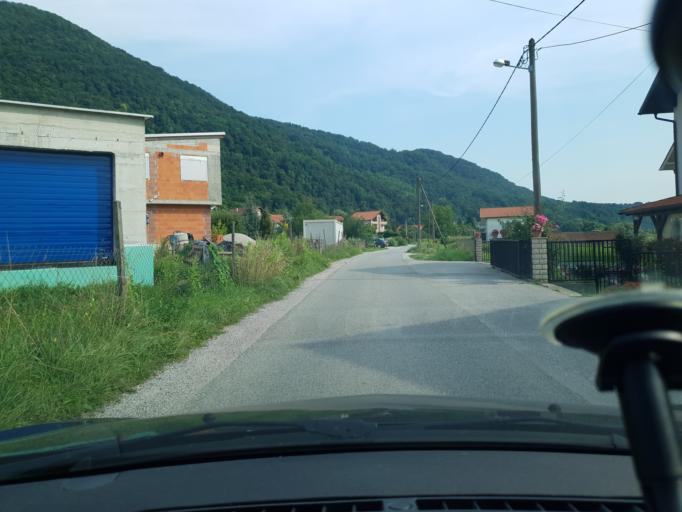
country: HR
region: Zagrebacka
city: Jablanovec
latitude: 45.8747
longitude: 15.8454
